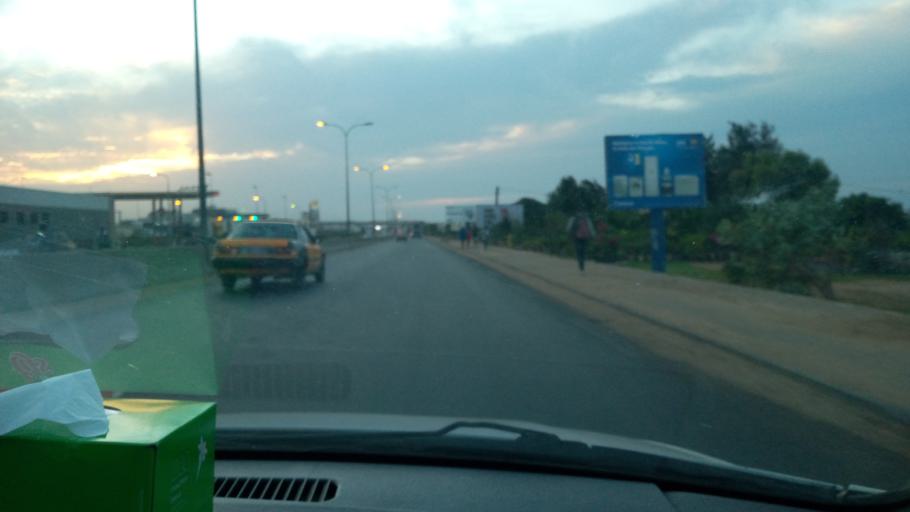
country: SN
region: Dakar
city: Pikine
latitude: 14.7467
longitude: -17.4107
